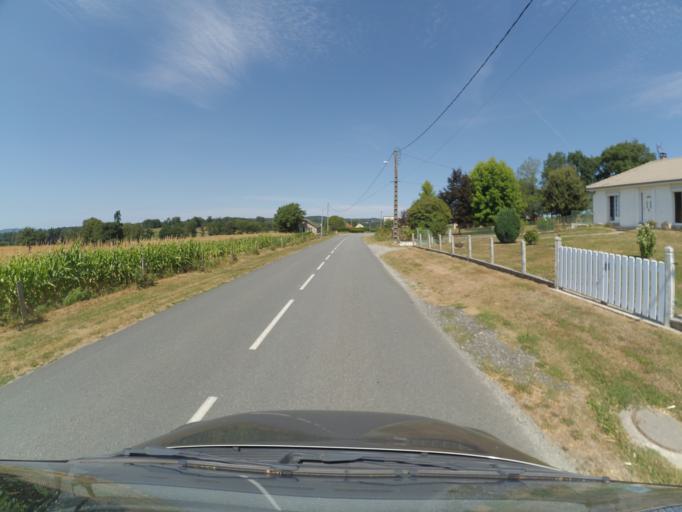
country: FR
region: Limousin
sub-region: Departement de la Creuse
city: Le Grand-Bourg
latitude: 46.0828
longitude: 1.6876
